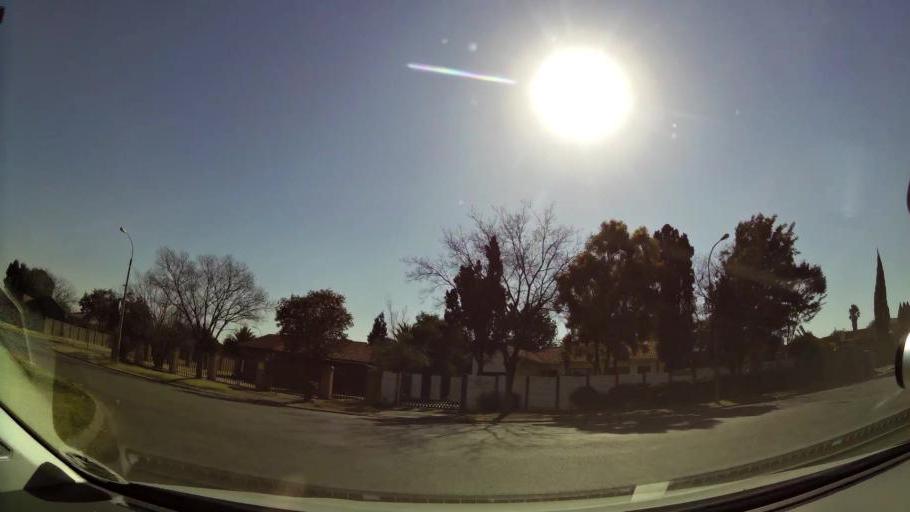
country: ZA
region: Gauteng
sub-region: Ekurhuleni Metropolitan Municipality
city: Tembisa
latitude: -26.0374
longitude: 28.2276
